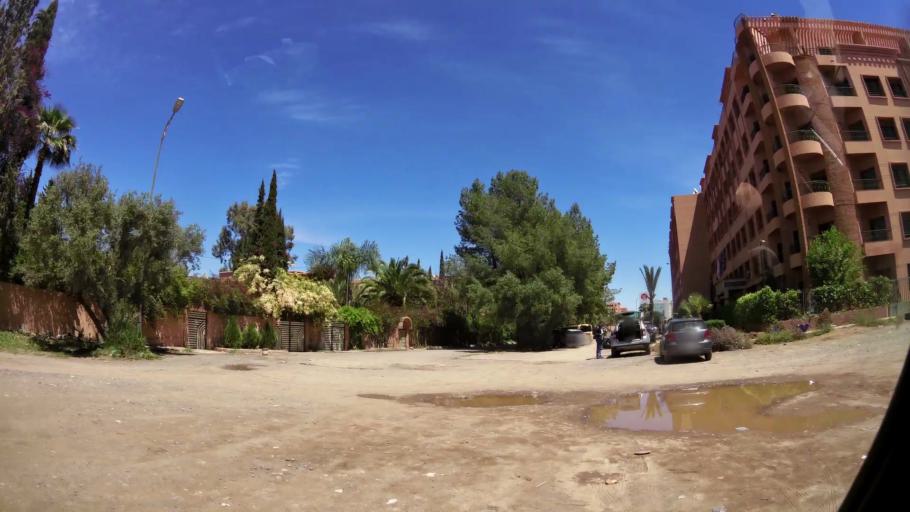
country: MA
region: Marrakech-Tensift-Al Haouz
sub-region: Marrakech
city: Marrakesh
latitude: 31.6209
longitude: -8.0146
